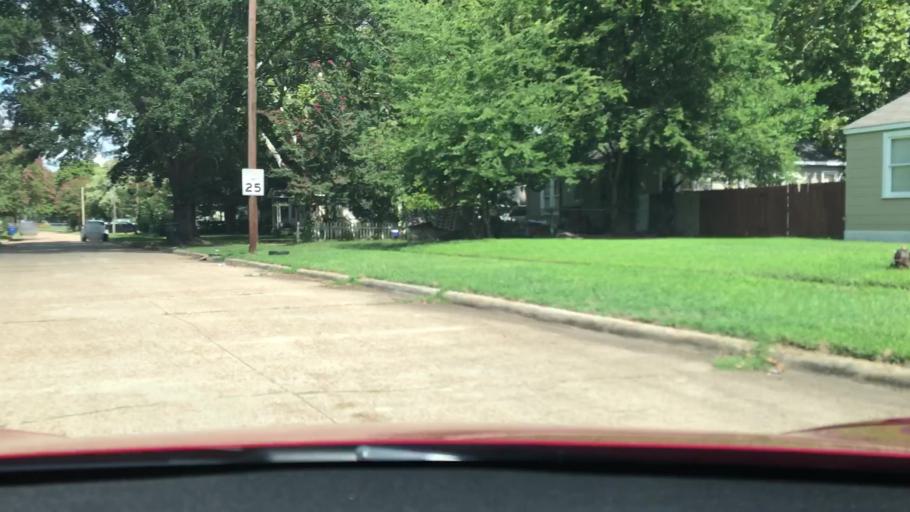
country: US
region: Louisiana
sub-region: Bossier Parish
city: Bossier City
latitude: 32.4736
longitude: -93.7312
